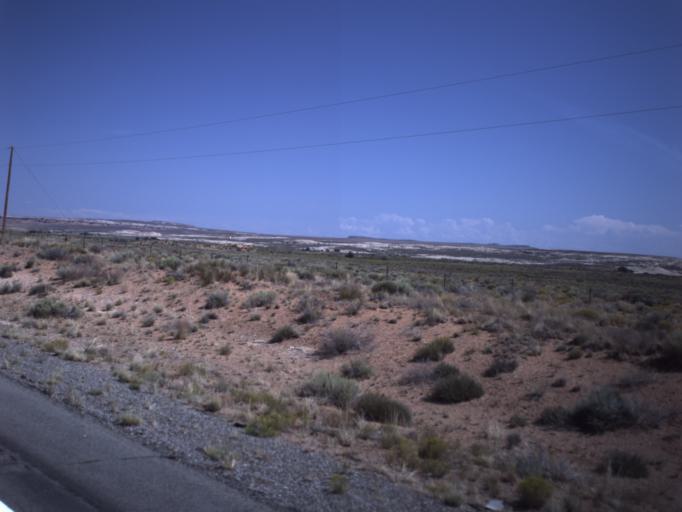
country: US
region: Utah
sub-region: San Juan County
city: Blanding
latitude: 37.0773
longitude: -109.5483
